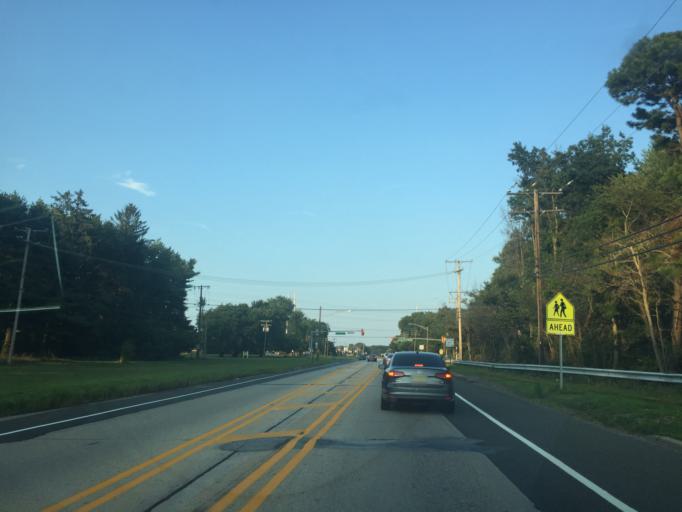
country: US
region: New Jersey
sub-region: Monmouth County
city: Shark River Hills
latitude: 40.2261
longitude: -74.0750
